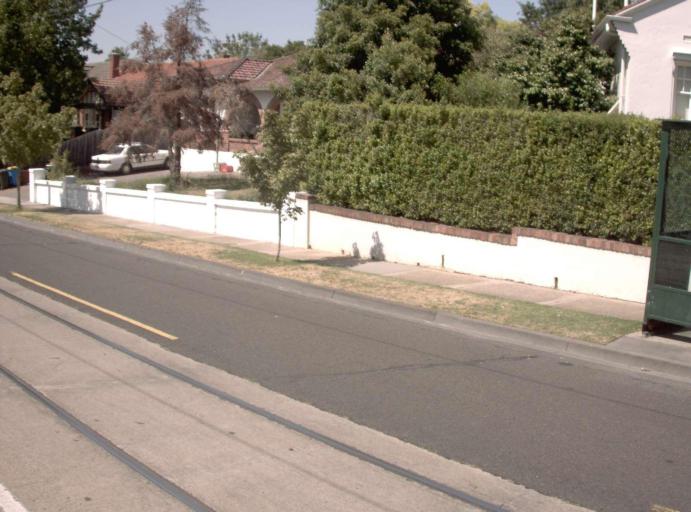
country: AU
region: Victoria
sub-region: Boroondara
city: Camberwell
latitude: -37.8397
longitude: 145.0663
